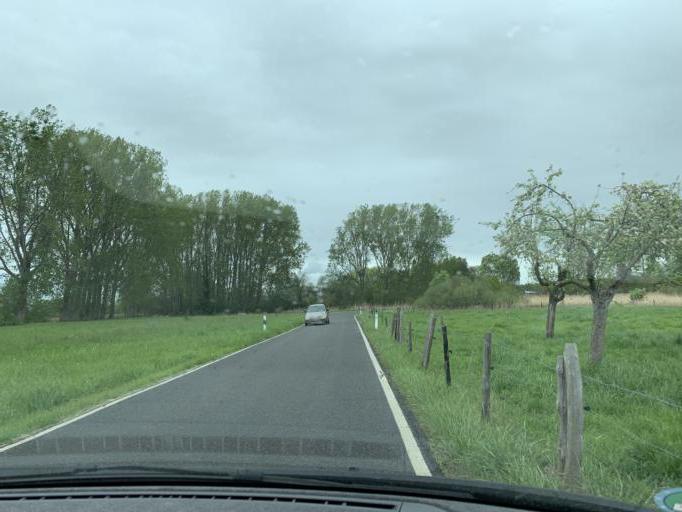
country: DE
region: North Rhine-Westphalia
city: Zulpich
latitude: 50.6606
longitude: 6.6594
